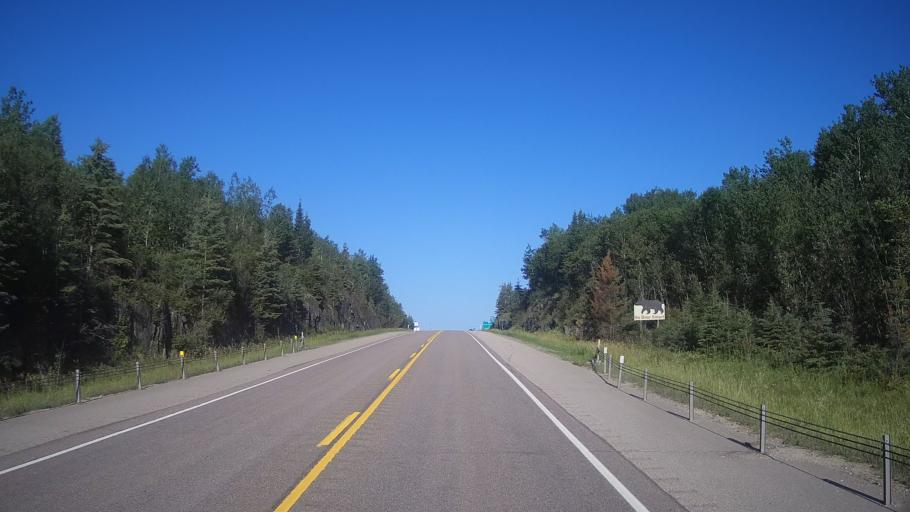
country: US
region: Minnesota
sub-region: Roseau County
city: Warroad
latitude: 49.7372
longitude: -95.2010
